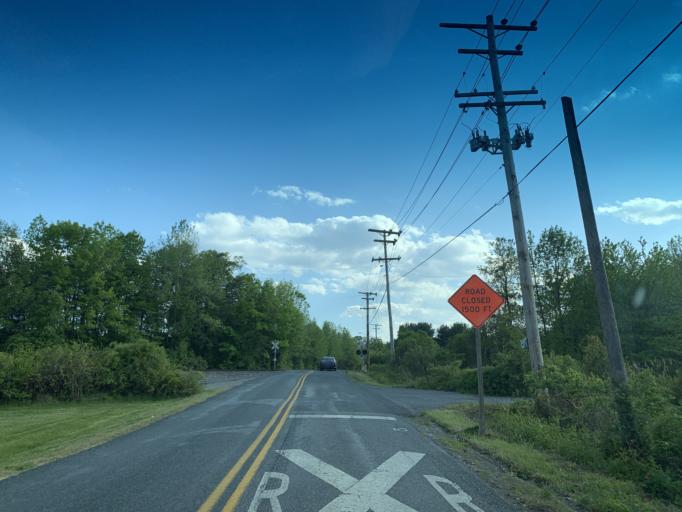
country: US
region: Maryland
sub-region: Harford County
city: Joppatowne
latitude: 39.4368
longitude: -76.3329
